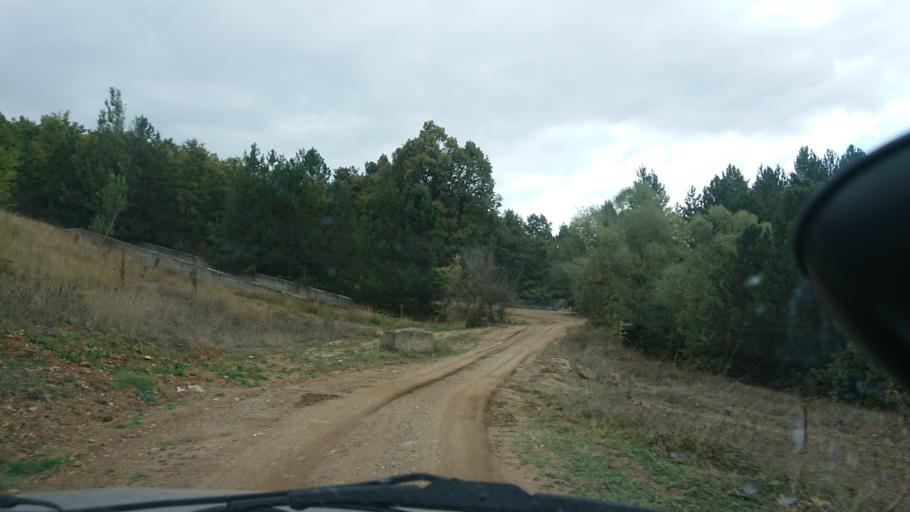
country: TR
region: Bilecik
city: Pazaryeri
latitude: 40.0169
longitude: 29.7974
